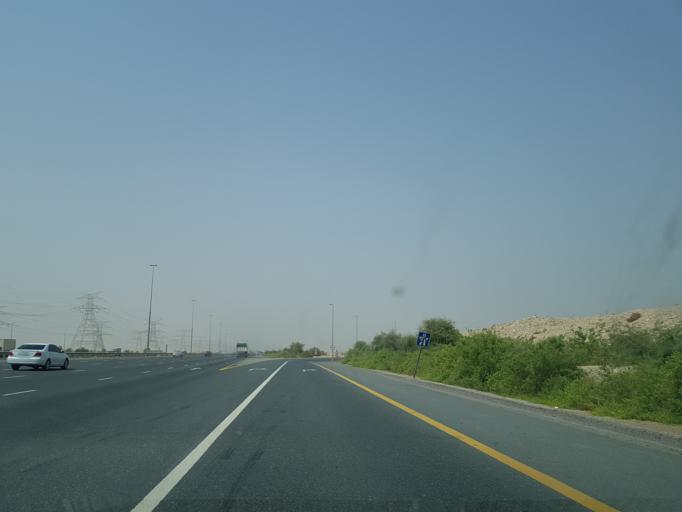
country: AE
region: Dubai
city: Dubai
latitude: 25.0527
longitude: 55.3120
